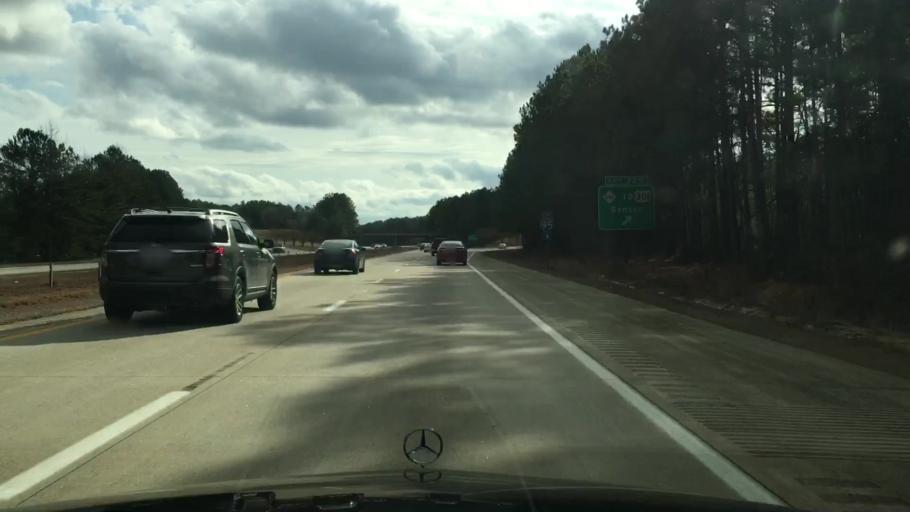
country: US
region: North Carolina
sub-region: Johnston County
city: Benson
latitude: 35.4272
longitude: -78.5315
